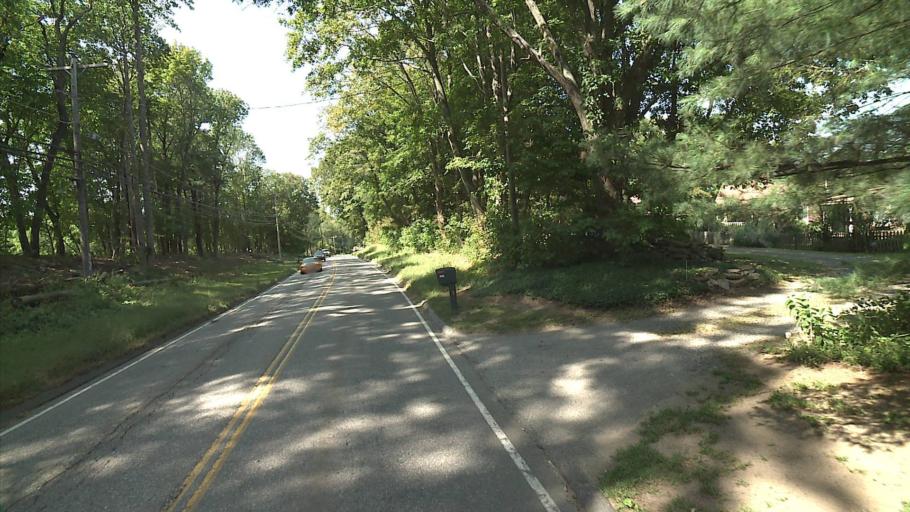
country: US
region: Connecticut
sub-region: Windham County
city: South Windham
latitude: 41.6304
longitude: -72.2033
